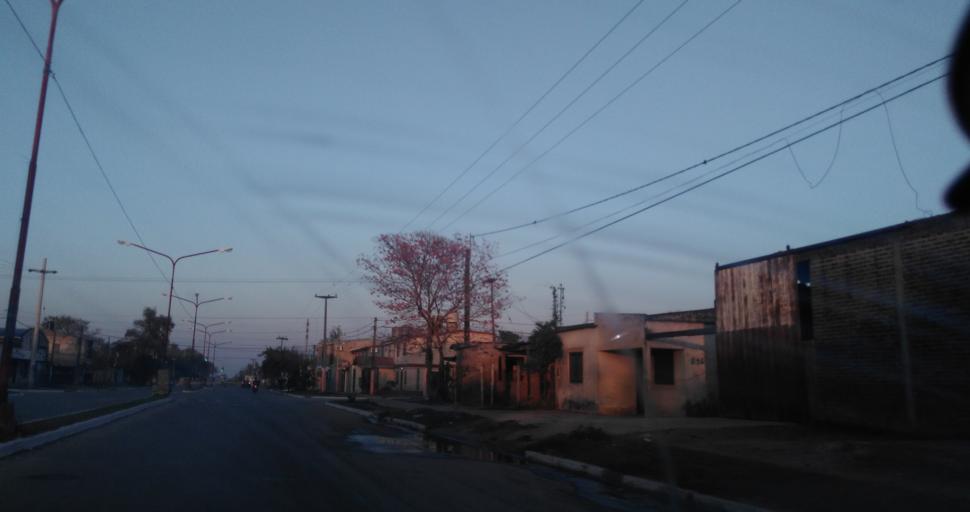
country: AR
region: Chaco
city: Resistencia
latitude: -27.4882
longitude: -58.9851
